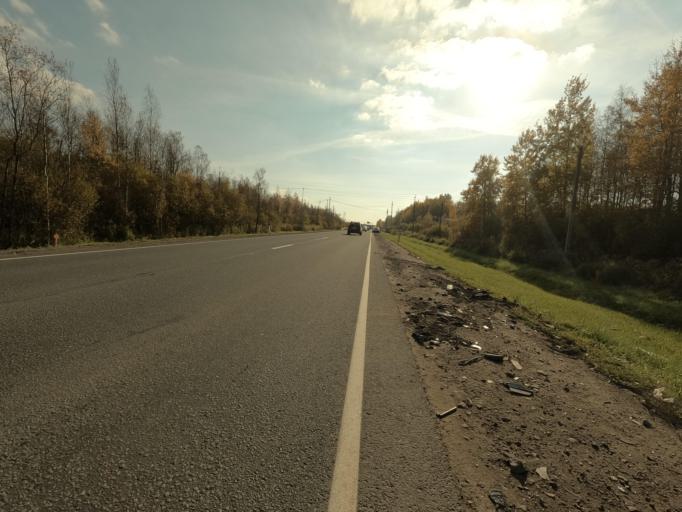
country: RU
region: Leningrad
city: Mga
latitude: 59.7648
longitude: 31.0954
